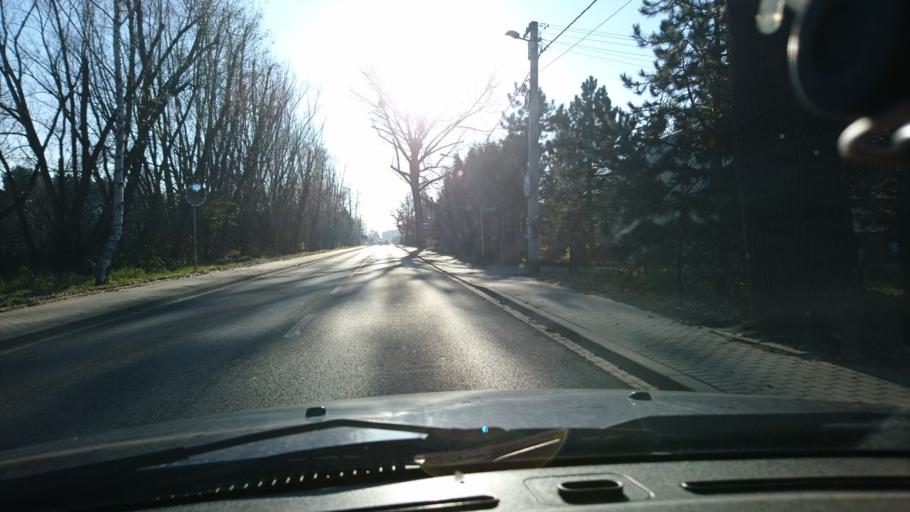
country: PL
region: Silesian Voivodeship
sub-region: Powiat bielski
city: Bestwina
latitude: 49.8608
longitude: 19.0482
